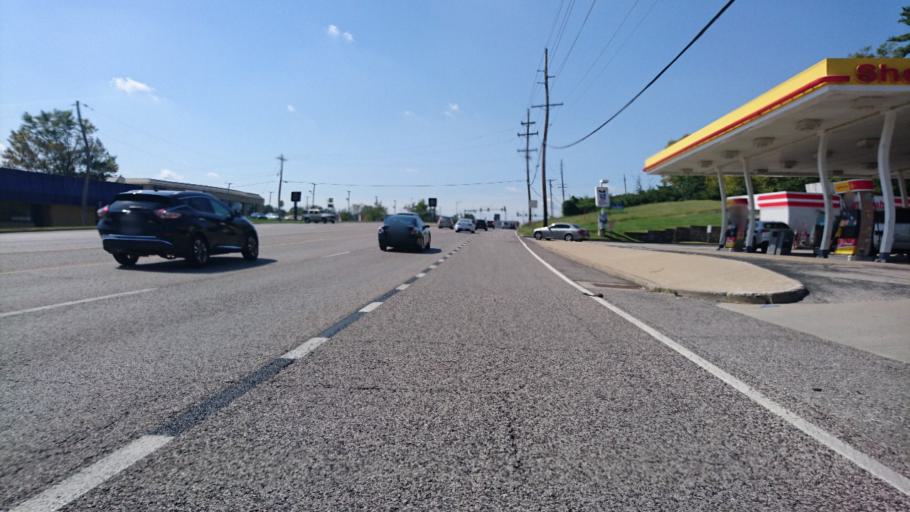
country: US
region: Missouri
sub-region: Saint Louis County
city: Town and Country
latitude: 38.5964
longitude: -90.4769
